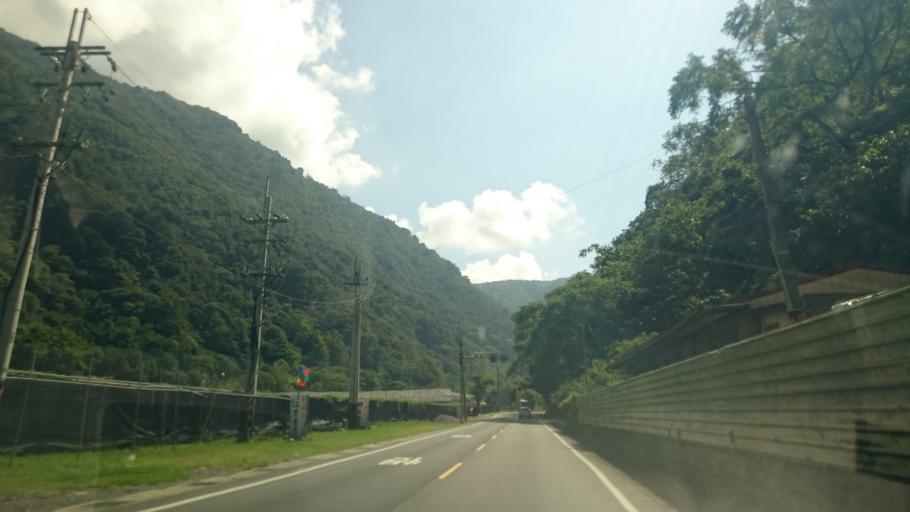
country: TW
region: Taiwan
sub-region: Nantou
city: Puli
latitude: 24.0030
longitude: 121.0541
